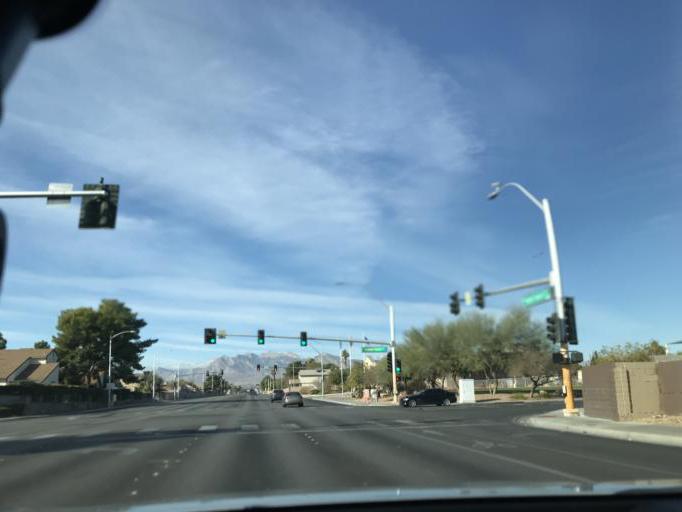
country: US
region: Nevada
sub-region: Clark County
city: Spring Valley
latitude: 36.2032
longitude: -115.2325
